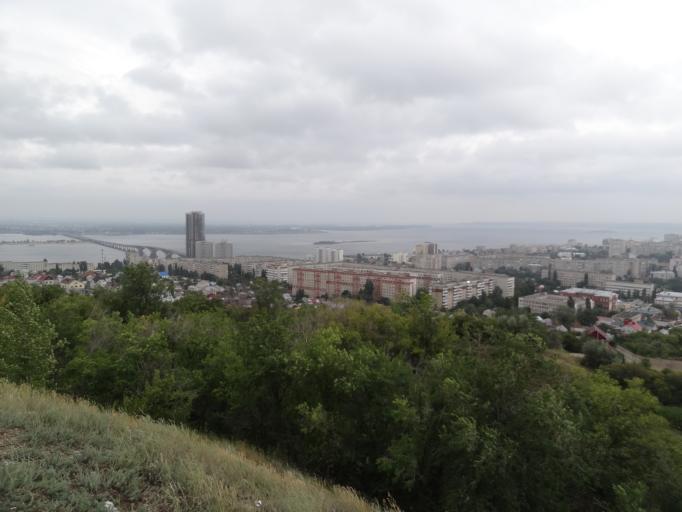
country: RU
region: Saratov
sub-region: Saratovskiy Rayon
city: Saratov
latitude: 51.5386
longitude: 46.0644
